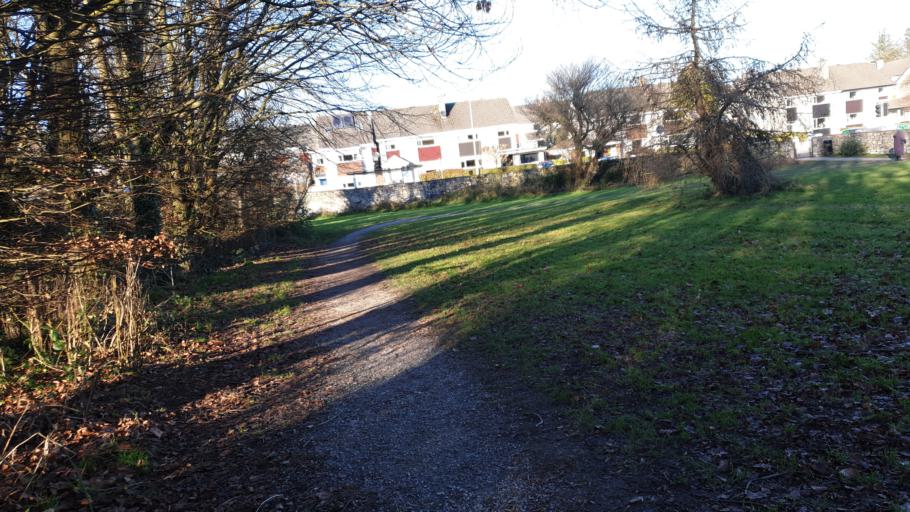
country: IE
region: Munster
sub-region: County Cork
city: Cork
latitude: 51.8867
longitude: -8.4242
